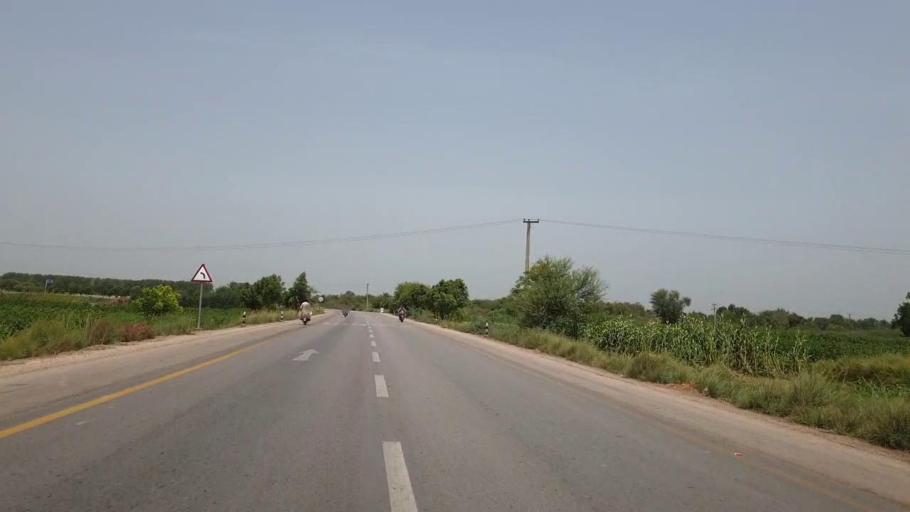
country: PK
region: Sindh
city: Nawabshah
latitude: 26.2450
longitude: 68.4643
